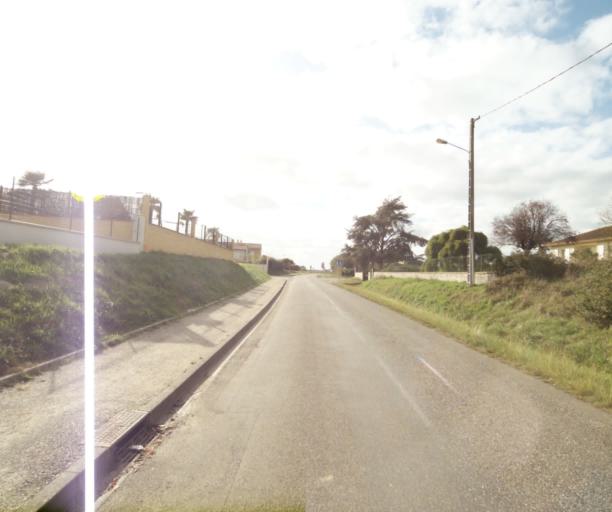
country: FR
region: Midi-Pyrenees
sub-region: Departement du Tarn-et-Garonne
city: Finhan
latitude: 43.8983
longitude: 1.1290
